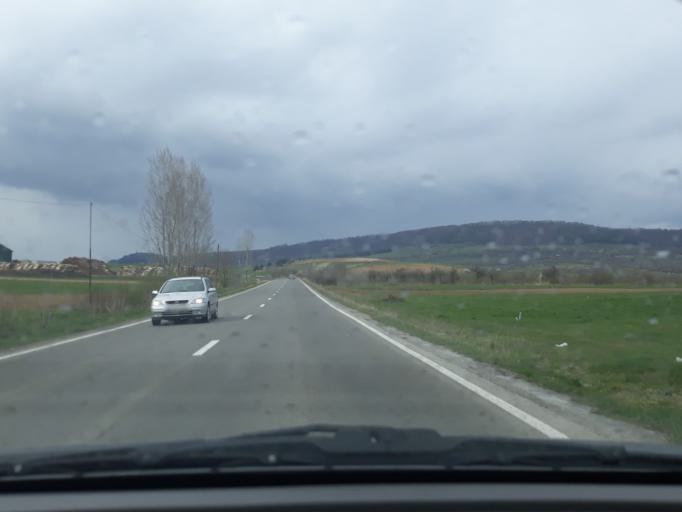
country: RO
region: Harghita
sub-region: Comuna Lupeni
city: Lupeni
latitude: 46.3886
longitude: 25.2164
